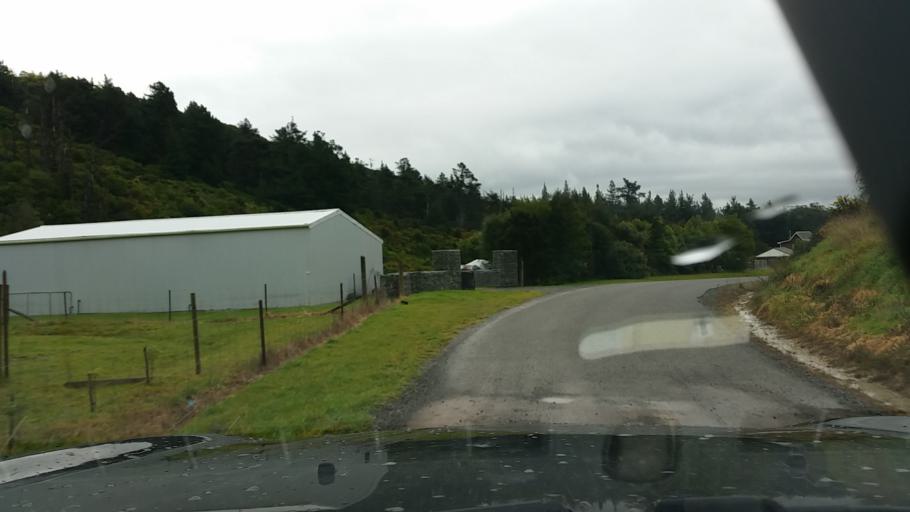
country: NZ
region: Marlborough
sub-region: Marlborough District
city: Picton
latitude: -41.2853
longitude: 174.0351
